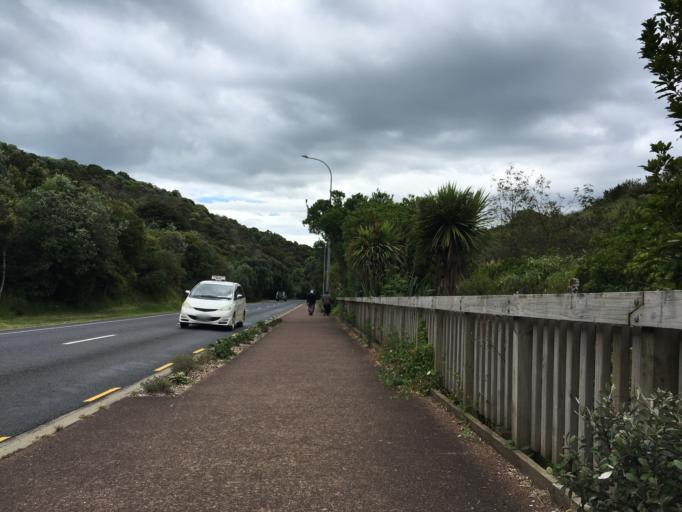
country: NZ
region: Auckland
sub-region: Auckland
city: Pakuranga
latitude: -36.7823
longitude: 175.0033
